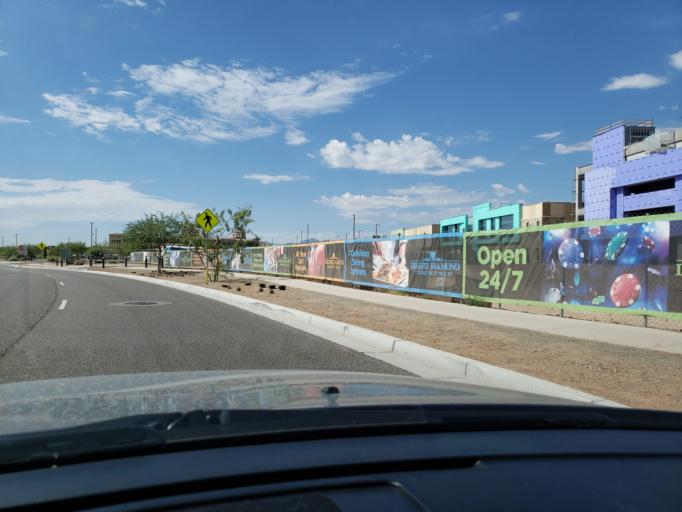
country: US
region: Arizona
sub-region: Maricopa County
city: Peoria
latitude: 33.5482
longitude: -112.2600
